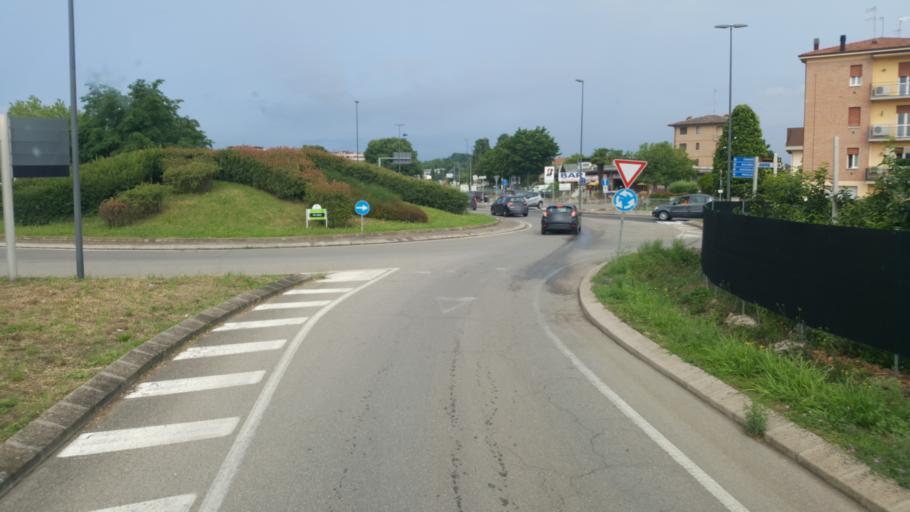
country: IT
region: Emilia-Romagna
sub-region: Provincia di Modena
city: Vignola
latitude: 44.4904
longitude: 11.0077
